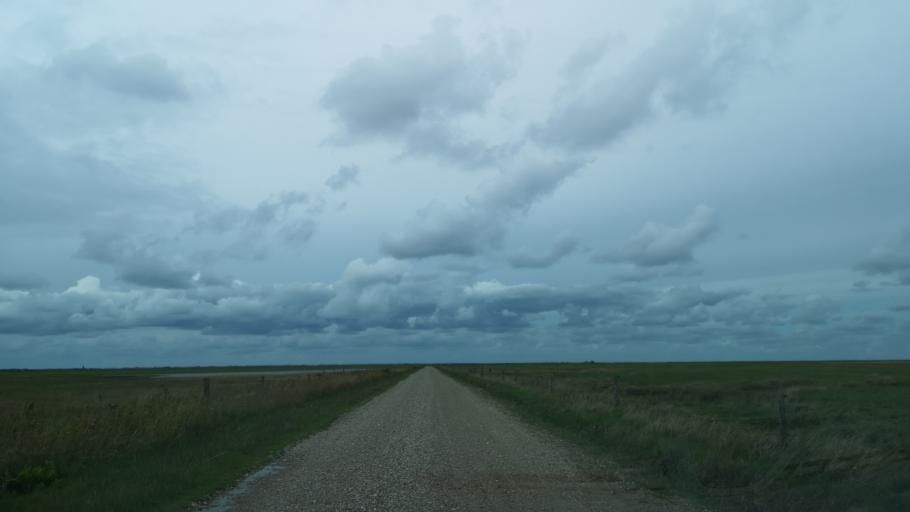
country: DK
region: Central Jutland
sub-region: Ringkobing-Skjern Kommune
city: Hvide Sande
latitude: 55.8636
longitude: 8.2353
